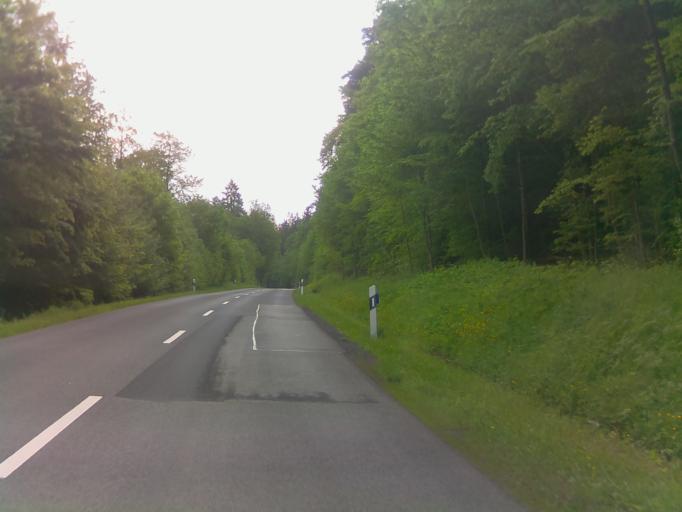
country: DE
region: Bavaria
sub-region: Regierungsbezirk Unterfranken
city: Hohenroth
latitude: 50.3532
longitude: 10.1426
